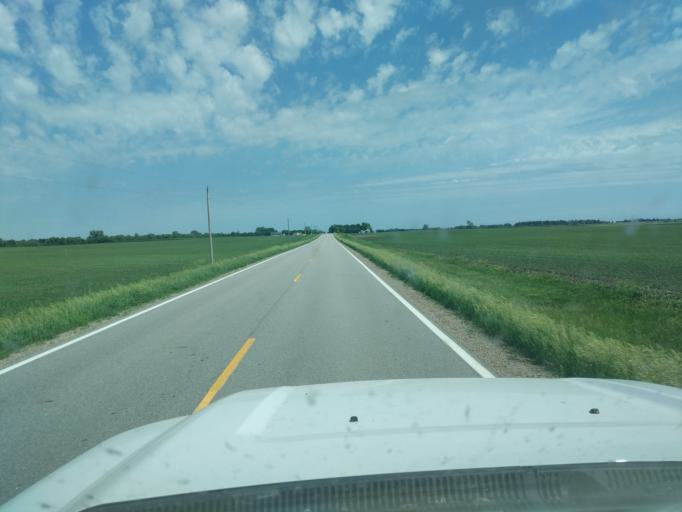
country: US
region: Minnesota
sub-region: Yellow Medicine County
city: Granite Falls
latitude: 44.7546
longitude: -95.4014
